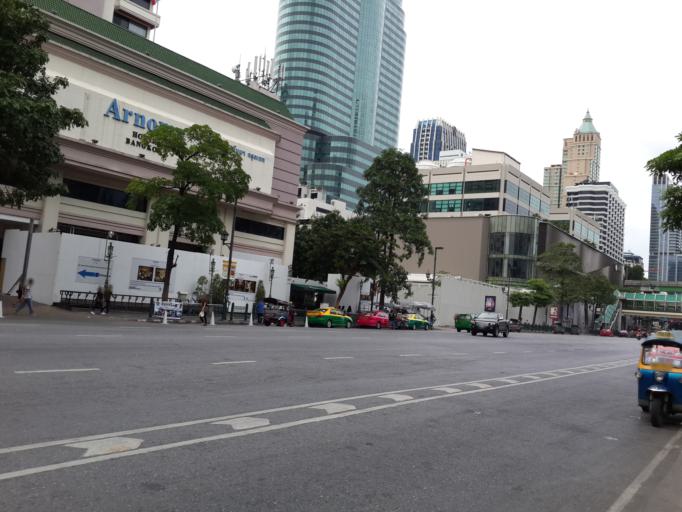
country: TH
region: Bangkok
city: Ratchathewi
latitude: 13.7469
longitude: 100.5405
